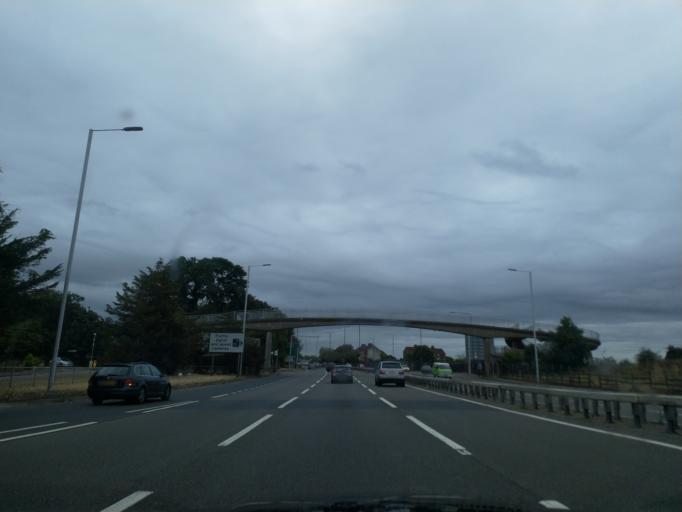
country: GB
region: England
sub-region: Greater London
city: Feltham
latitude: 51.4313
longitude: -0.3991
